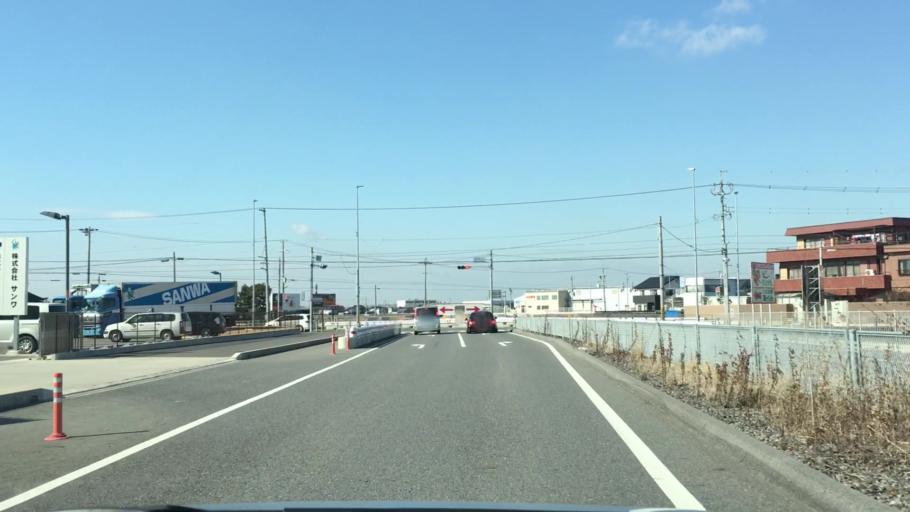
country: JP
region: Aichi
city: Anjo
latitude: 34.9947
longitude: 137.1118
